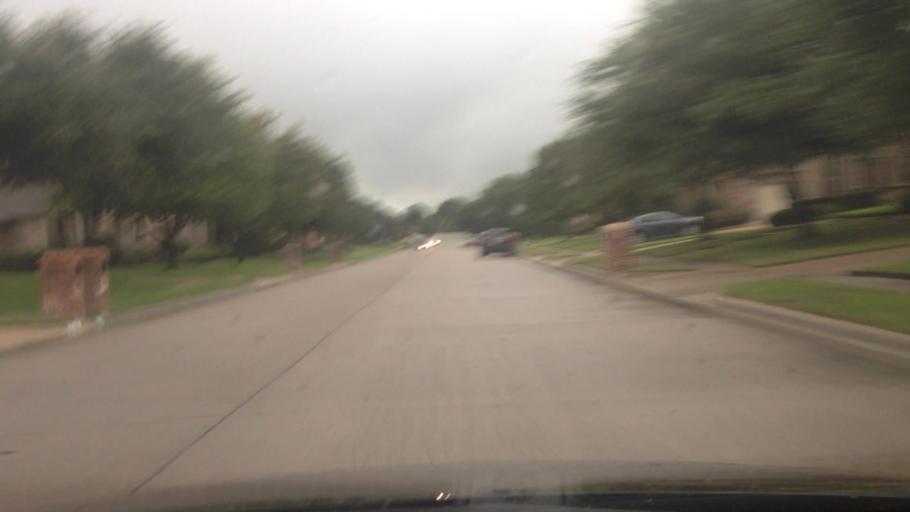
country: US
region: Texas
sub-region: Tarrant County
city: Colleyville
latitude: 32.8822
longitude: -97.1759
